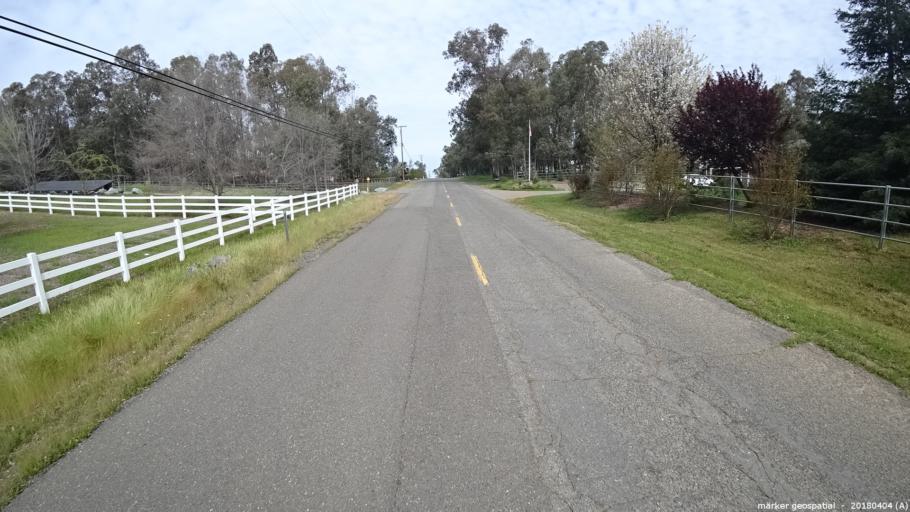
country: US
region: California
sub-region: Sacramento County
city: Clay
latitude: 38.3291
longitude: -121.1452
